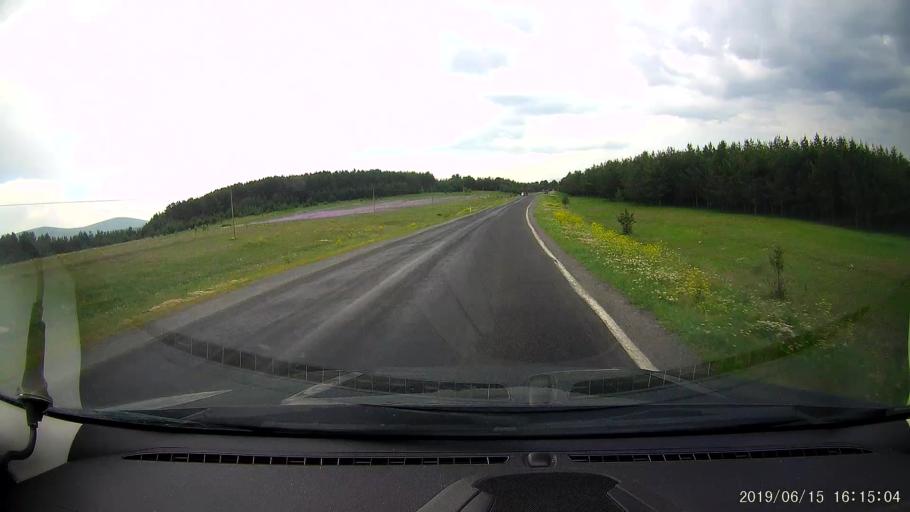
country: TR
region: Ardahan
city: Hanak
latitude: 41.2726
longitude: 42.8527
